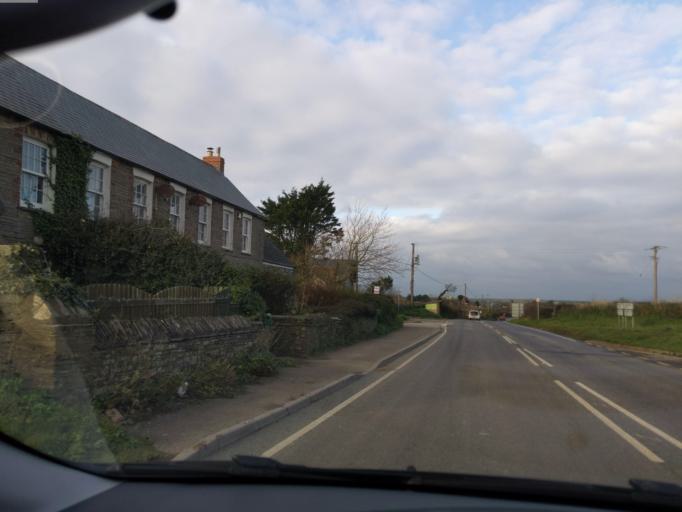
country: GB
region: England
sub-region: Cornwall
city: Padstow
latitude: 50.5140
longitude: -4.9491
